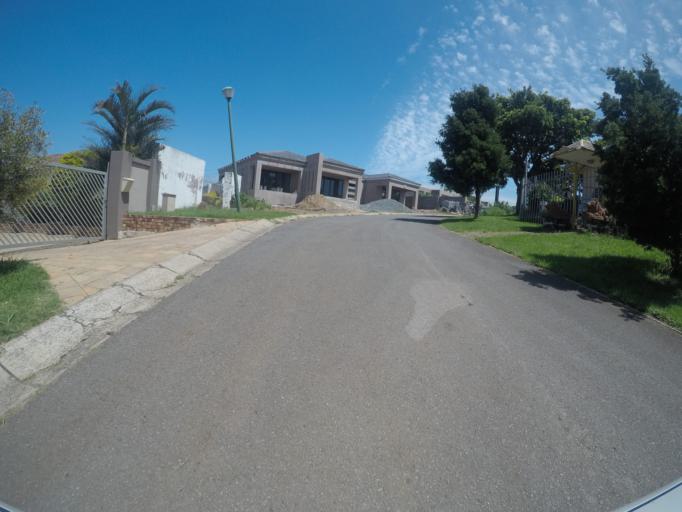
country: ZA
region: Eastern Cape
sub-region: Buffalo City Metropolitan Municipality
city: East London
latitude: -32.9421
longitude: 27.9968
